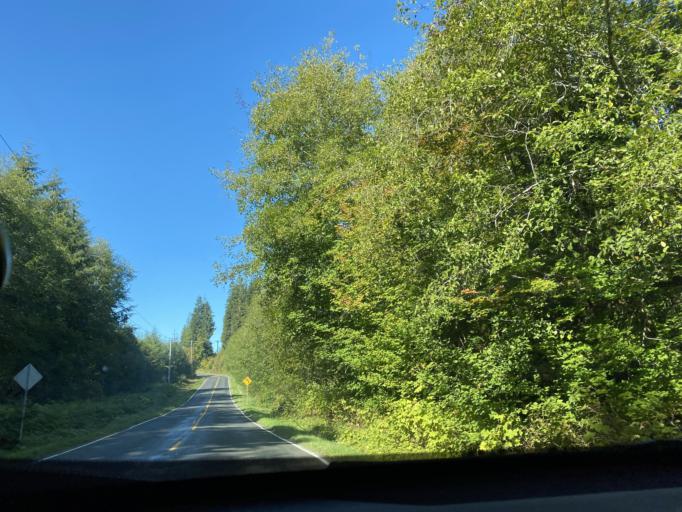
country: US
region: Washington
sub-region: Clallam County
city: Forks
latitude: 47.9481
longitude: -124.5034
